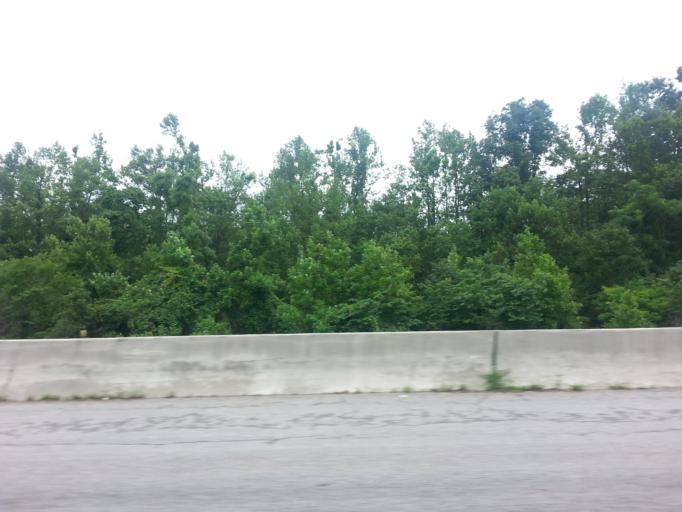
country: US
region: Tennessee
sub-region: Putnam County
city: Monterey
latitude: 36.1332
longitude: -85.3410
